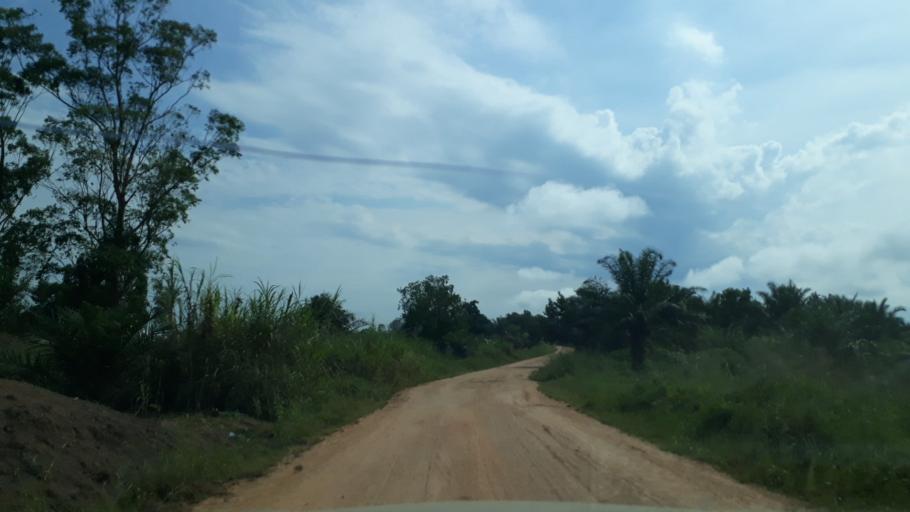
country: CD
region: Eastern Province
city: Bunia
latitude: 1.3968
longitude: 29.8047
